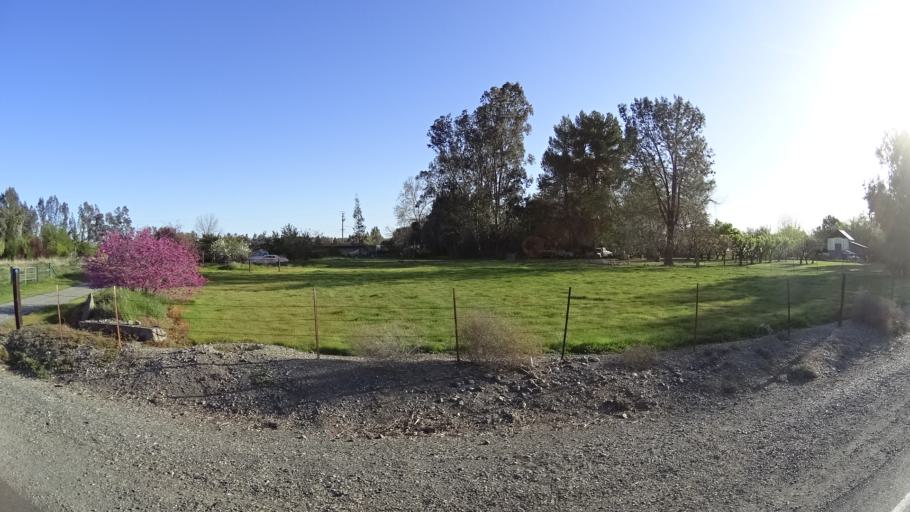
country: US
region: California
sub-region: Glenn County
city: Orland
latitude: 39.7537
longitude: -122.2127
